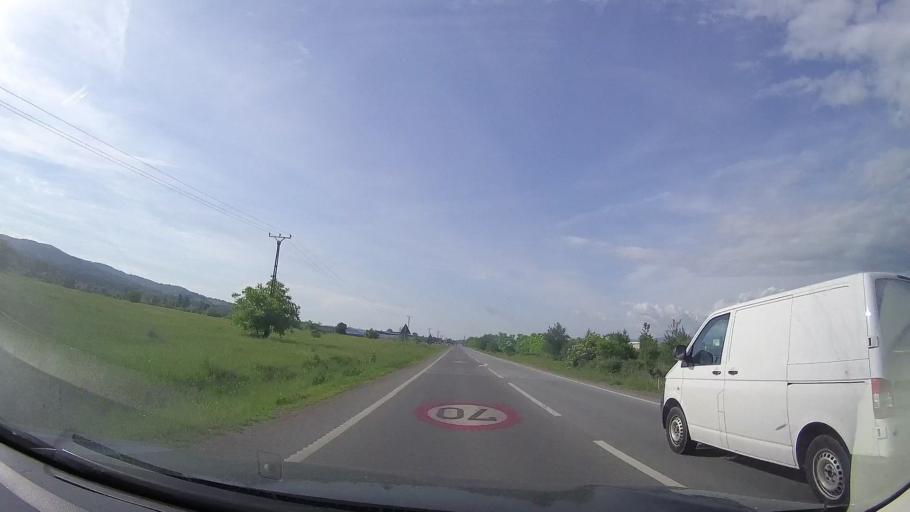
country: RO
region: Caras-Severin
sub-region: Comuna Buchin
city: Buchin
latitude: 45.3755
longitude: 22.2357
